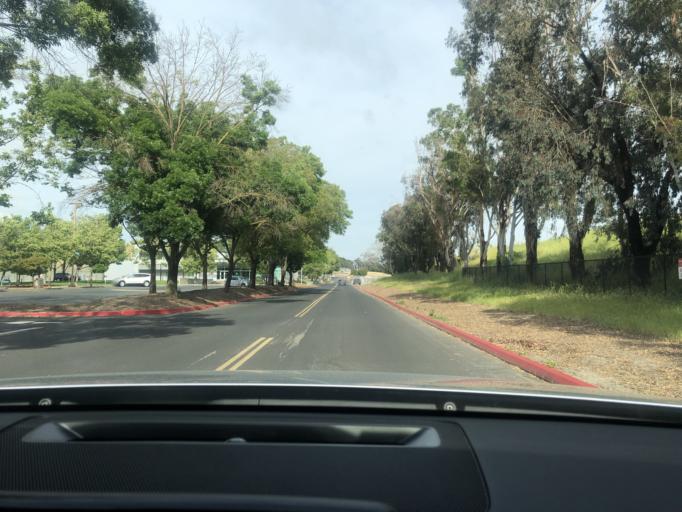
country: US
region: California
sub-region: Alameda County
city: Dublin
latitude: 37.7159
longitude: -121.8859
